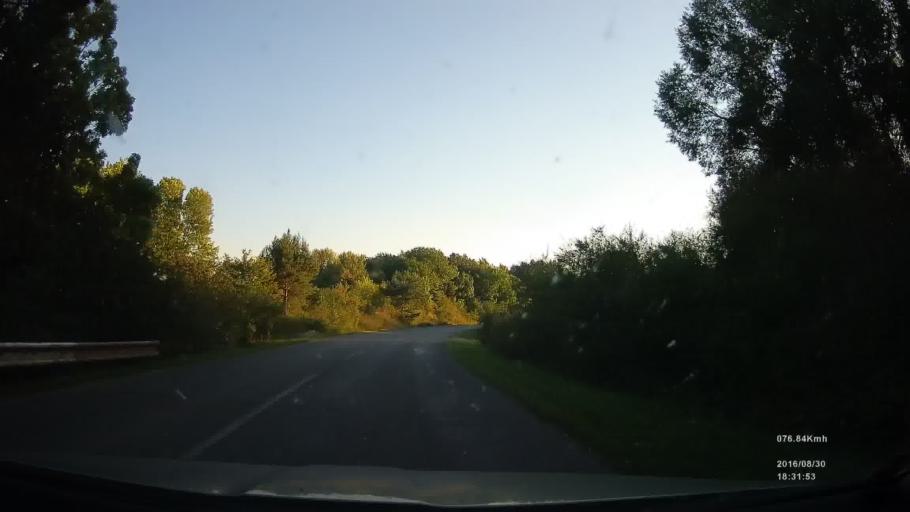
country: SK
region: Zilinsky
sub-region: Okres Liptovsky Mikulas
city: Liptovsky Mikulas
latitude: 49.1224
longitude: 19.5025
